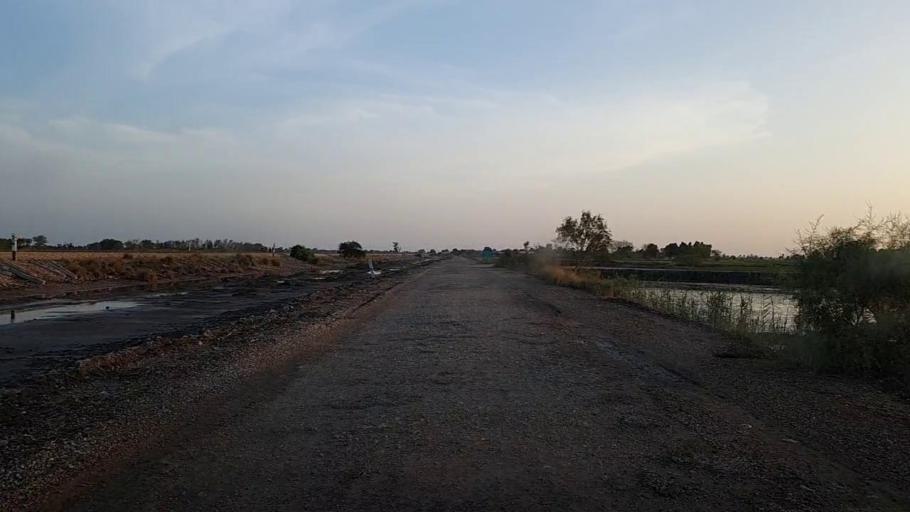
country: PK
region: Sindh
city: Karaundi
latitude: 27.0520
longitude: 68.3876
